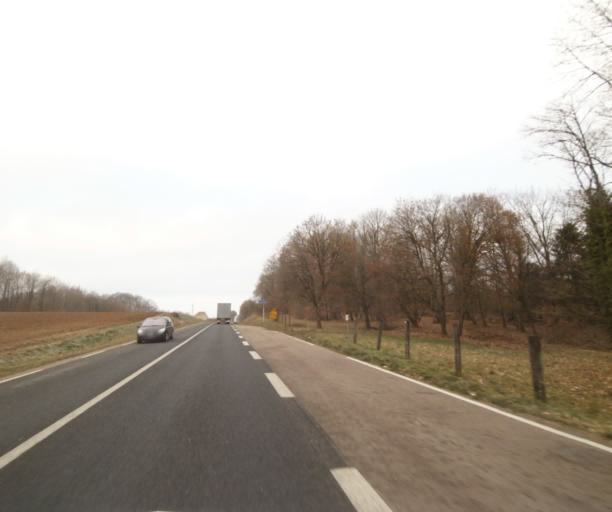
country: FR
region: Lorraine
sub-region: Departement de la Meuse
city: Ancerville
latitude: 48.6374
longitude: 5.0021
